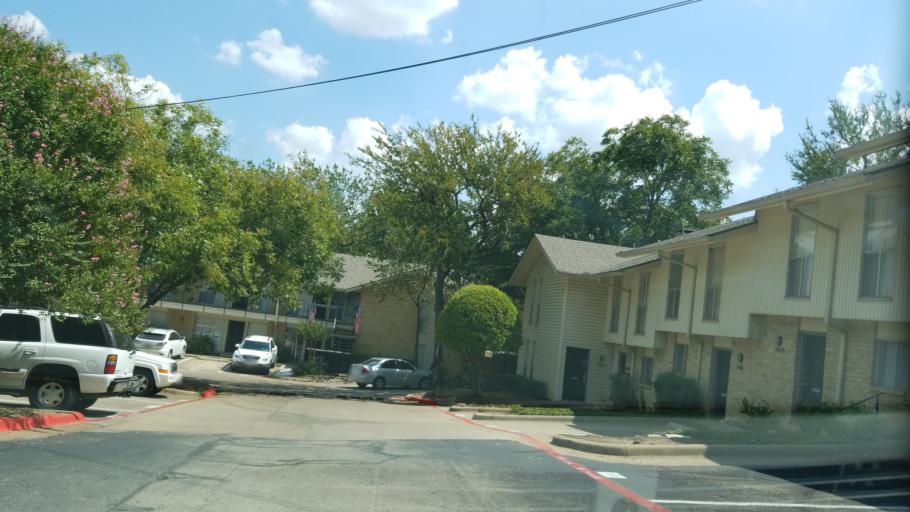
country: US
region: Texas
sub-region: Dallas County
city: Cockrell Hill
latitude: 32.7625
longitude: -96.8486
